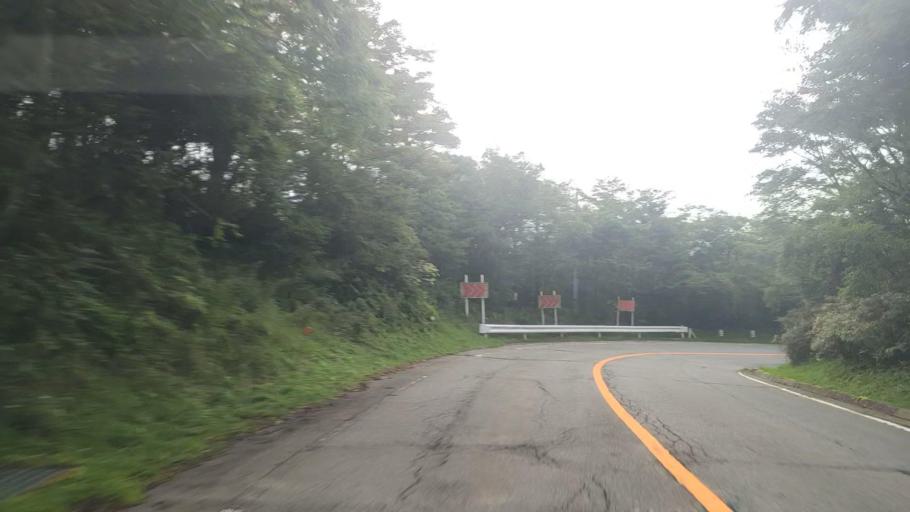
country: JP
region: Shizuoka
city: Fuji
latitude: 35.2961
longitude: 138.7741
